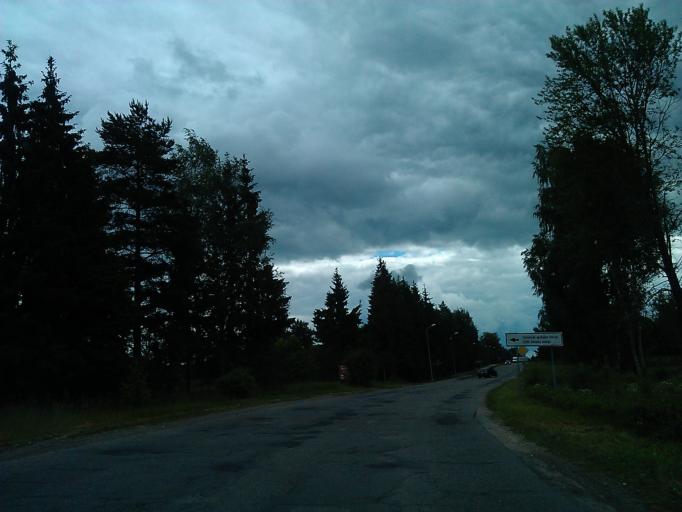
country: LV
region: Dobeles Rajons
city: Dobele
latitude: 56.6382
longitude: 23.2571
